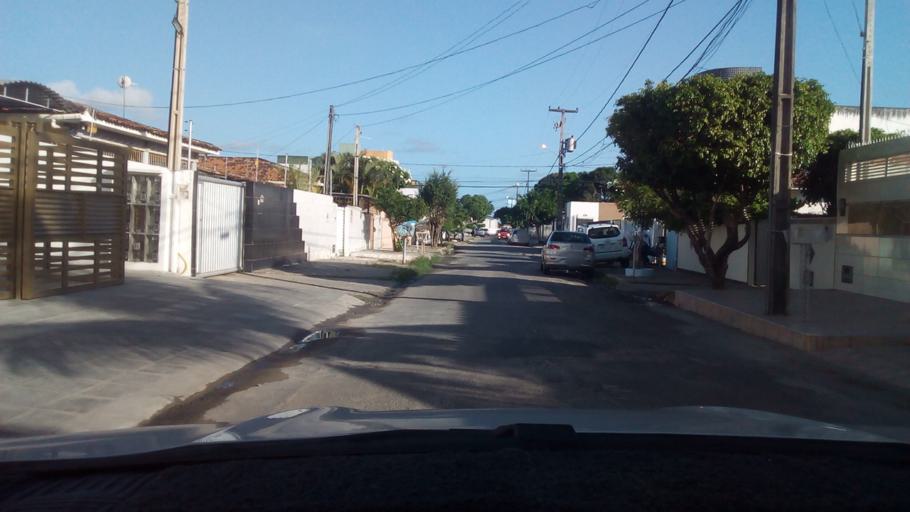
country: BR
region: Paraiba
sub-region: Joao Pessoa
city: Joao Pessoa
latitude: -7.1726
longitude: -34.8592
